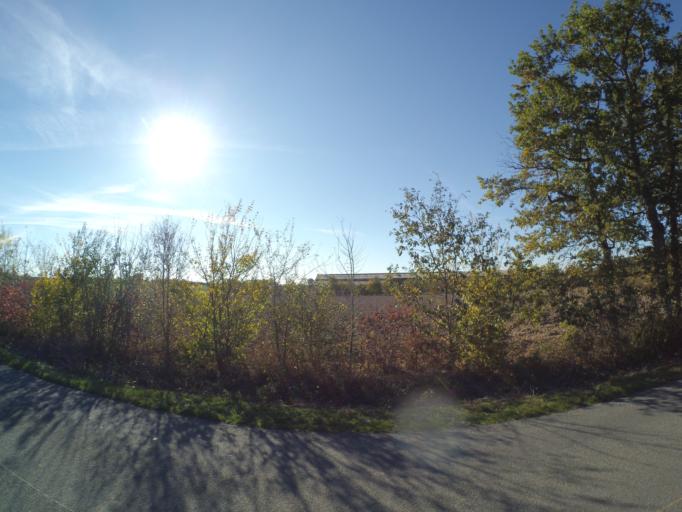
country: FR
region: Pays de la Loire
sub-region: Departement de la Loire-Atlantique
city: Saint-Lumine-de-Clisson
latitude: 47.0761
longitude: -1.3281
